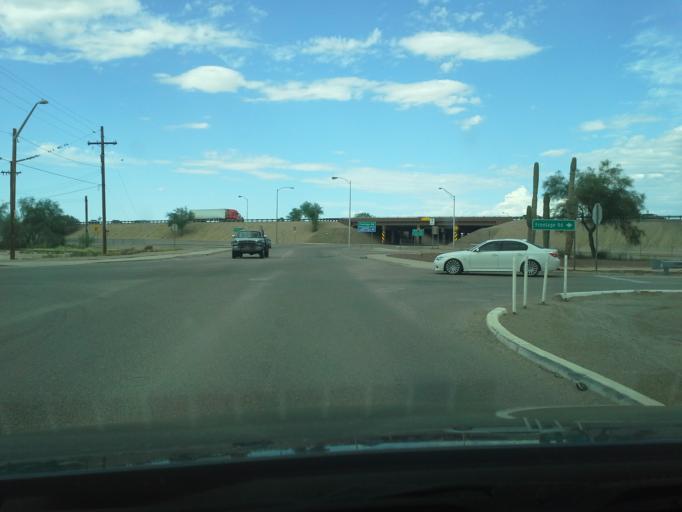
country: US
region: Arizona
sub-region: Pima County
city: Marana
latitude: 32.4604
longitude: -111.2170
